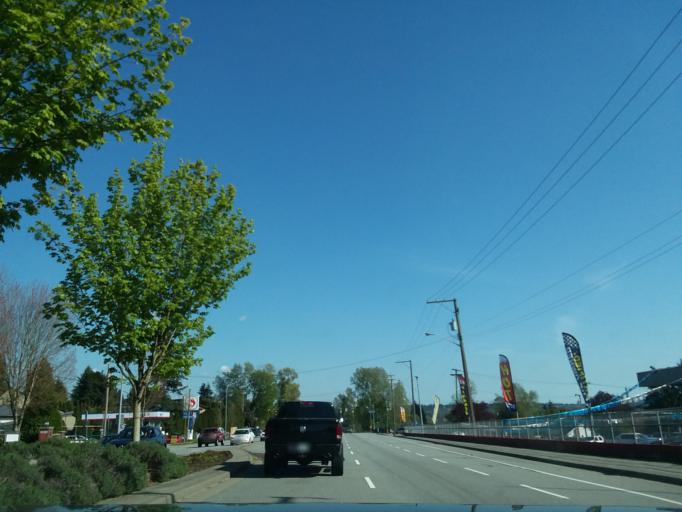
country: CA
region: British Columbia
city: New Westminster
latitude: 49.2407
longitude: -122.8833
